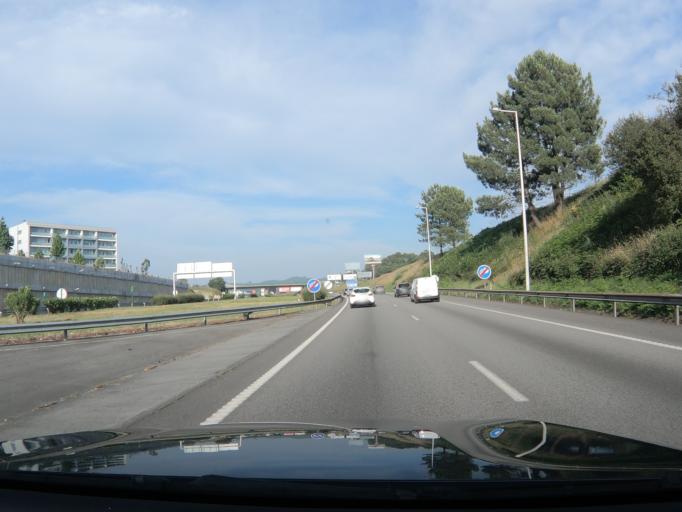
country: PT
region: Porto
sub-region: Maia
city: Pedroucos
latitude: 41.1969
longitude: -8.5808
